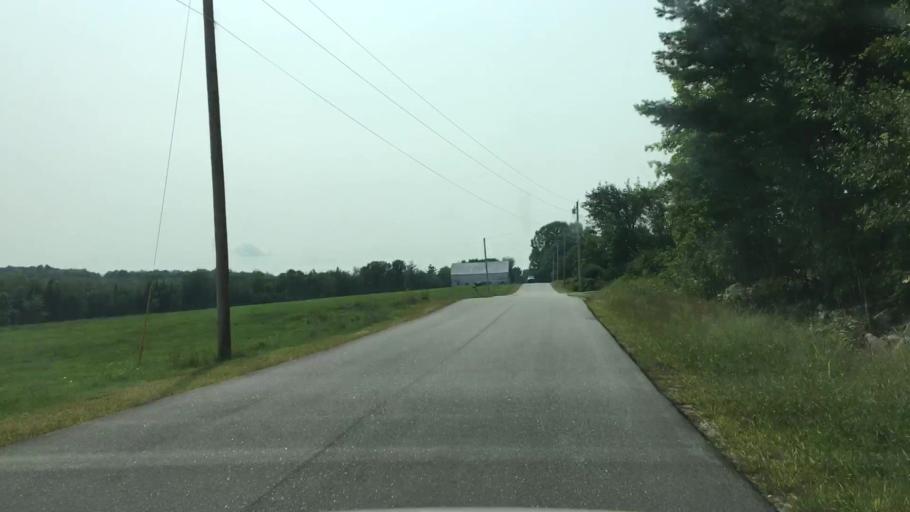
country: US
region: Maine
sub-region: Oxford County
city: Buckfield
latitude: 44.2991
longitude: -70.3144
